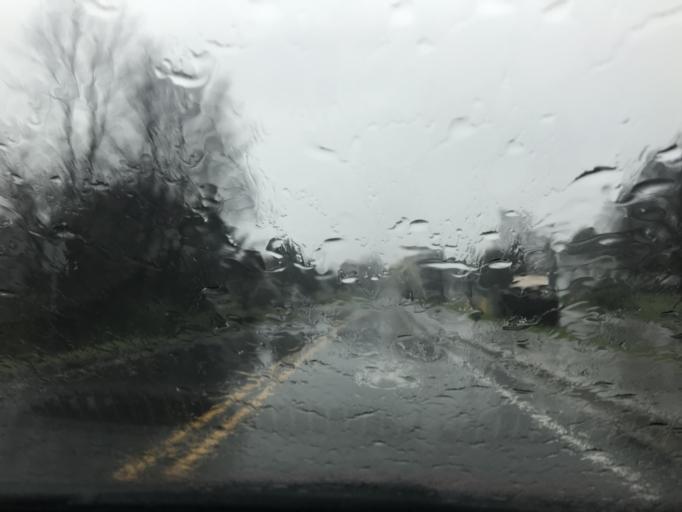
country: US
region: Indiana
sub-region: Clark County
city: Clarksville
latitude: 38.2829
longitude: -85.7609
